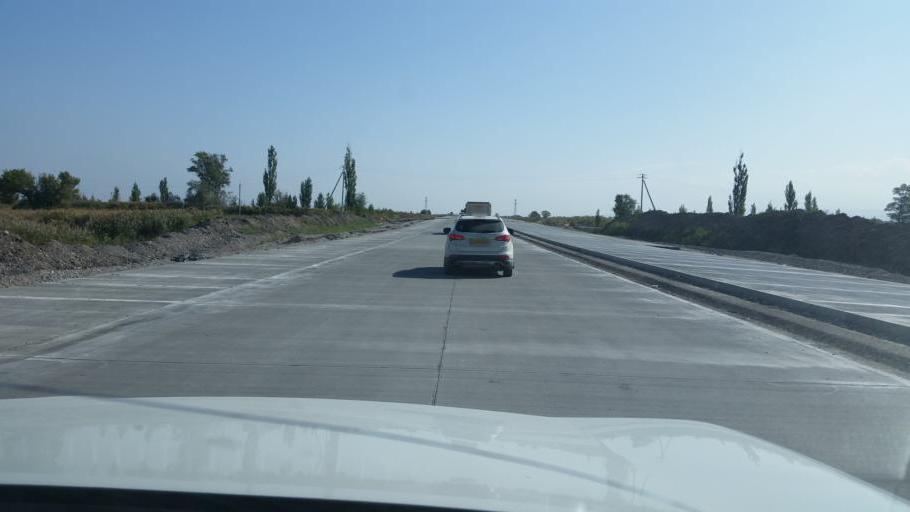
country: KZ
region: Almaty Oblysy
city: Turgen'
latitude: 43.5308
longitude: 77.5918
